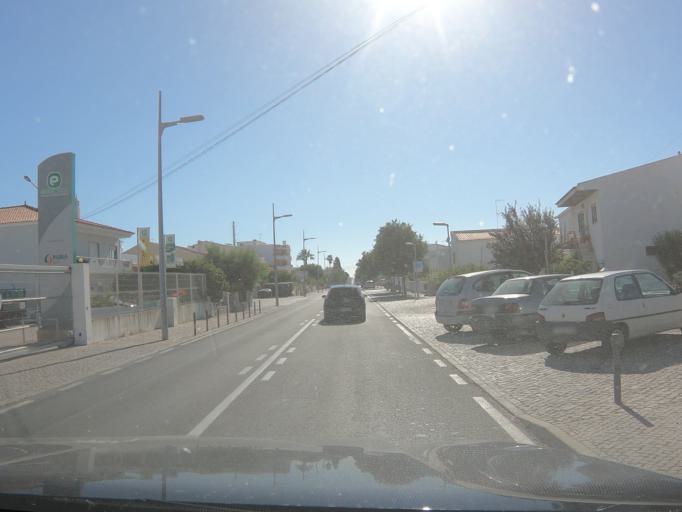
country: PT
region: Faro
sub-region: Loule
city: Loule
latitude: 37.1376
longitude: -8.0025
